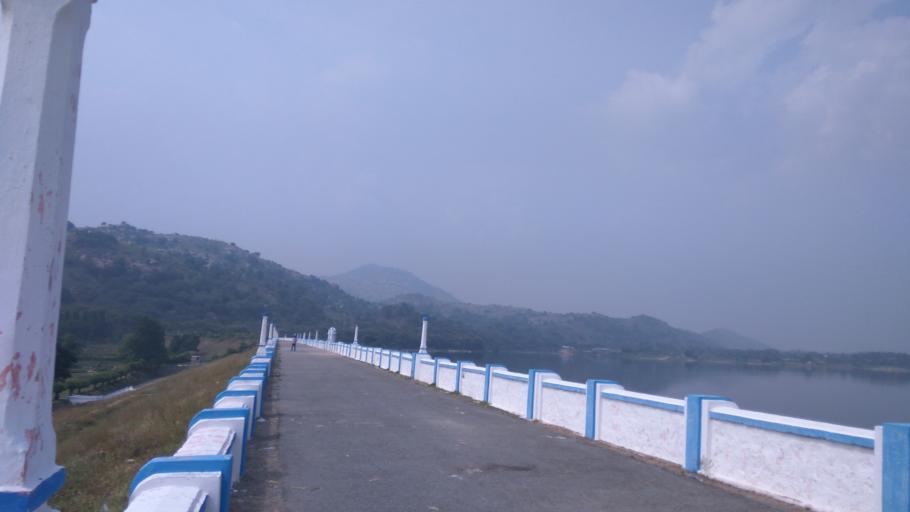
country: IN
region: Tamil Nadu
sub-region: Krishnagiri
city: Krishnagiri
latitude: 12.4755
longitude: 78.1852
